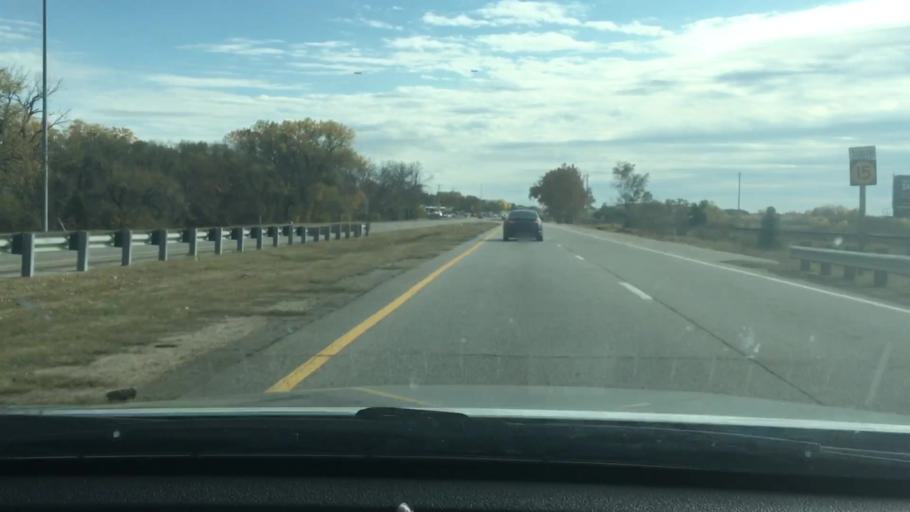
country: US
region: Kansas
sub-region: Sedgwick County
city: Wichita
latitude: 37.6383
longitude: -97.3066
